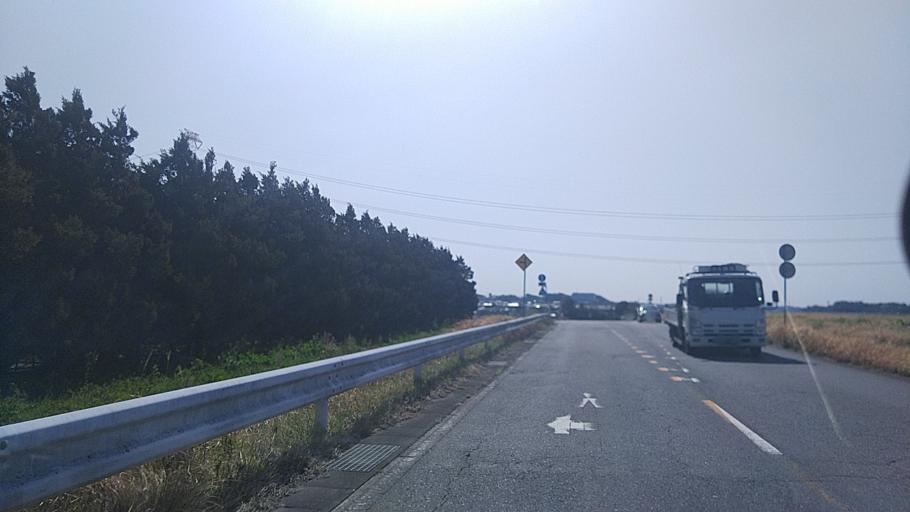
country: JP
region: Ibaraki
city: Fujishiro
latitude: 35.8702
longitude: 140.1301
